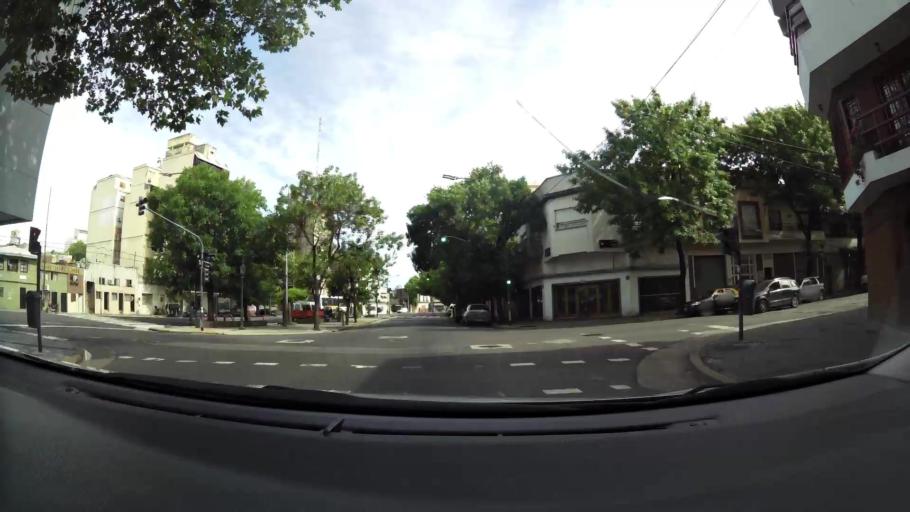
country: AR
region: Buenos Aires F.D.
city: Buenos Aires
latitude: -34.6415
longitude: -58.4165
